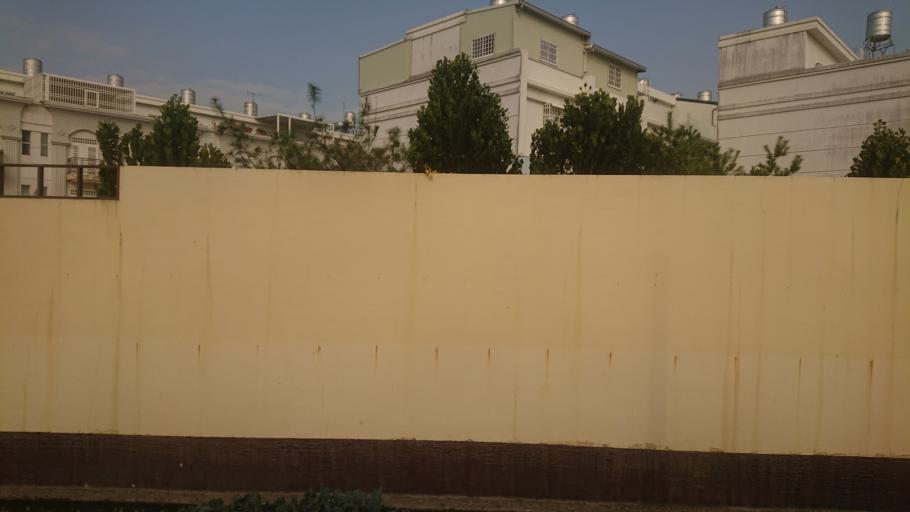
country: TW
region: Taiwan
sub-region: Yunlin
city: Douliu
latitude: 23.7058
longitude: 120.5323
